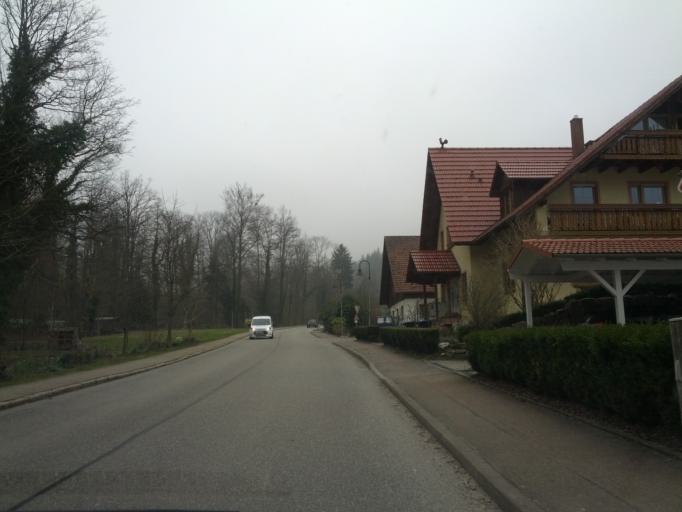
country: DE
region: Baden-Wuerttemberg
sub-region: Freiburg Region
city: Horben
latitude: 47.9399
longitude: 7.8673
